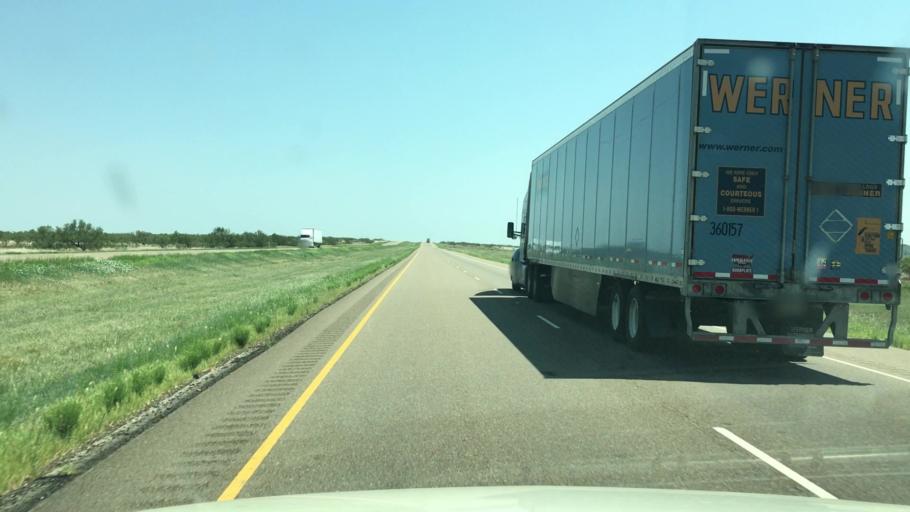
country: US
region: Texas
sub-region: Oldham County
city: Vega
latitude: 35.2222
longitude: -102.8831
